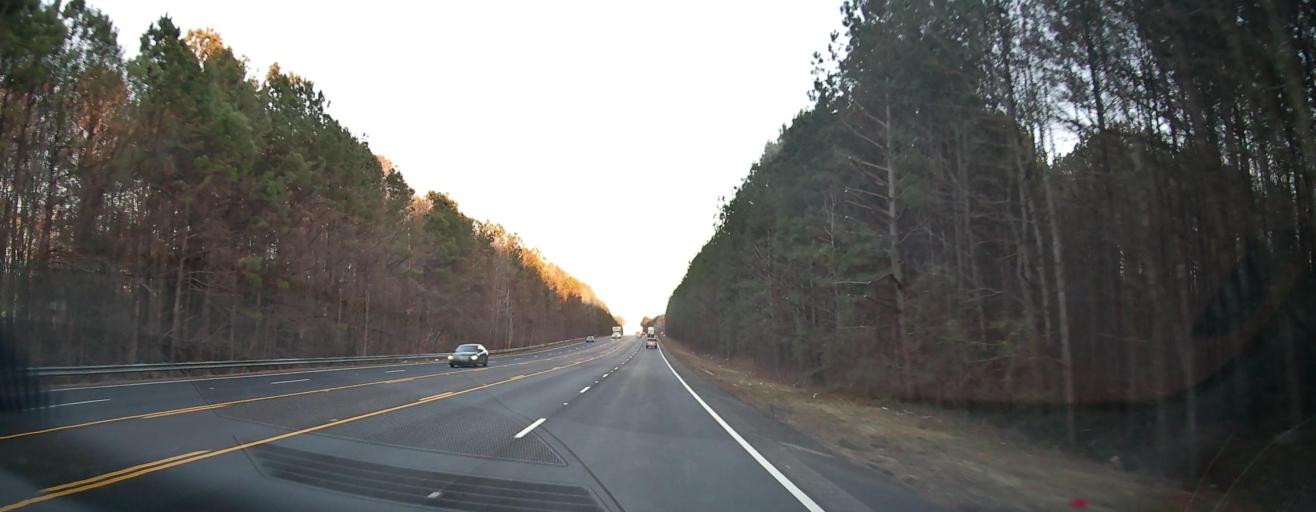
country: US
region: Georgia
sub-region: Clayton County
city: Riverdale
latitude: 33.5515
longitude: -84.4769
